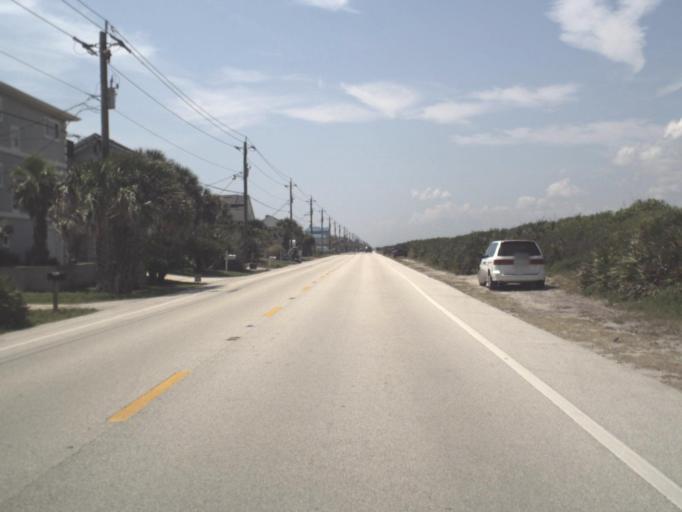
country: US
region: Florida
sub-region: Saint Johns County
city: Villano Beach
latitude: 30.0171
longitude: -81.3219
